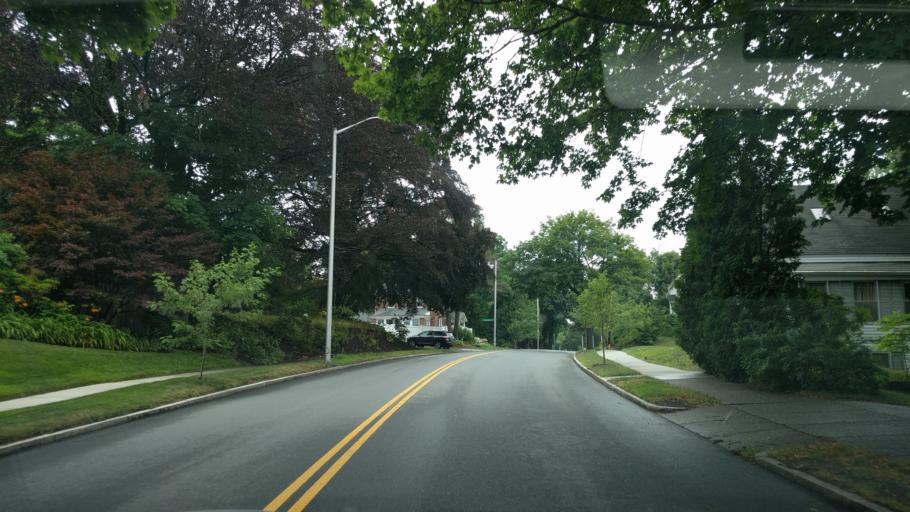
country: US
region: Massachusetts
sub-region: Worcester County
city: Worcester
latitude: 42.2829
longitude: -71.8149
